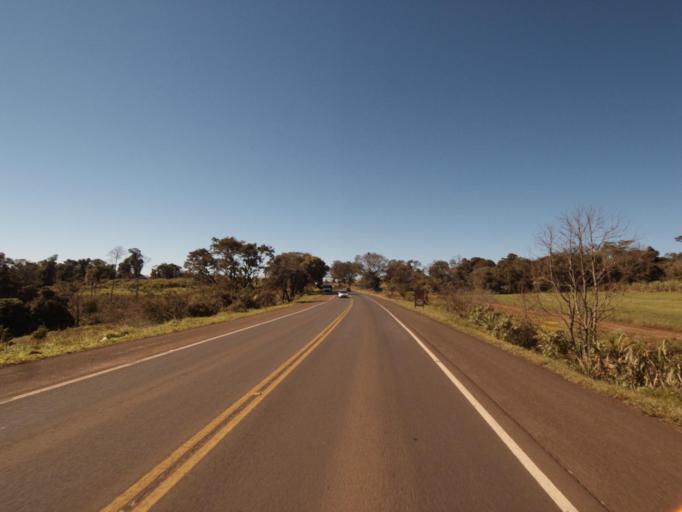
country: BR
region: Santa Catarina
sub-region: Chapeco
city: Chapeco
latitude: -26.9052
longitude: -52.8981
